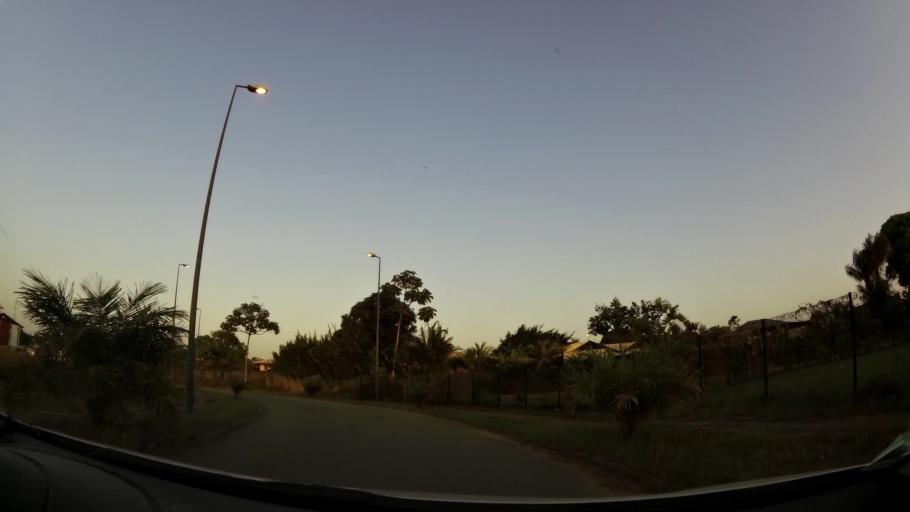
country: GF
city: Macouria
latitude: 4.9292
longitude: -52.4061
